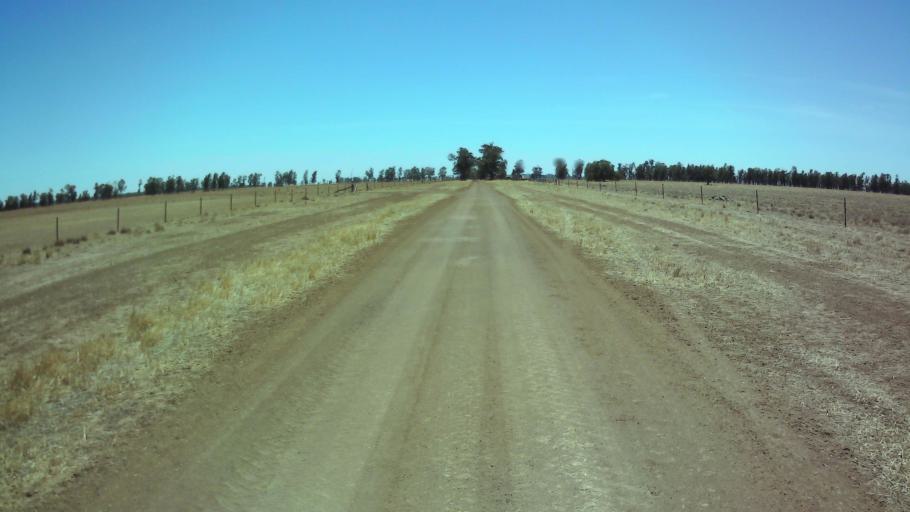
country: AU
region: New South Wales
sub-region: Weddin
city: Grenfell
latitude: -33.9754
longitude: 147.7372
